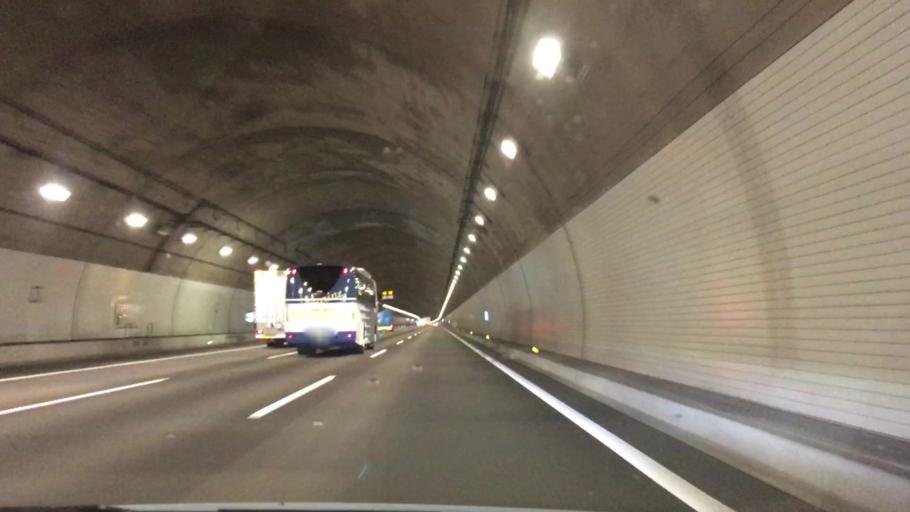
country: JP
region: Shizuoka
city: Fujieda
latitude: 34.9492
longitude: 138.2829
